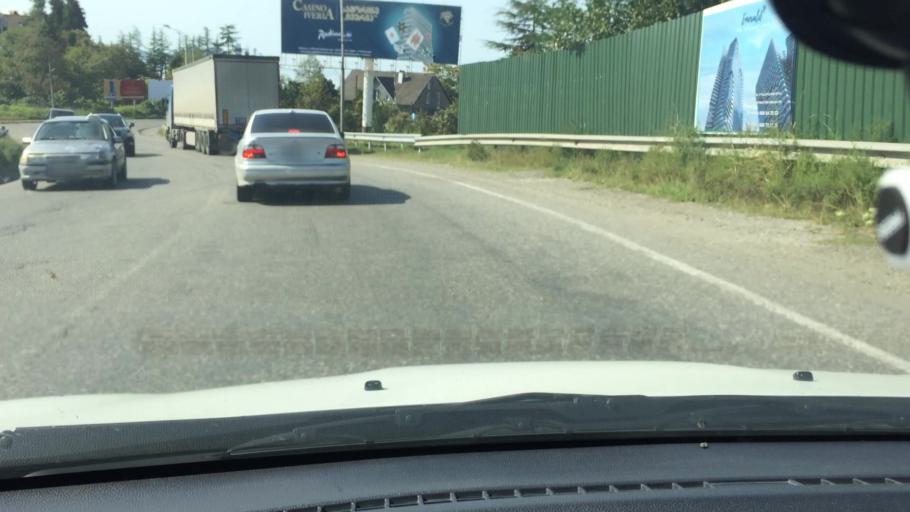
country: GE
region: Ajaria
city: Makhinjauri
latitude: 41.6868
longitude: 41.7040
